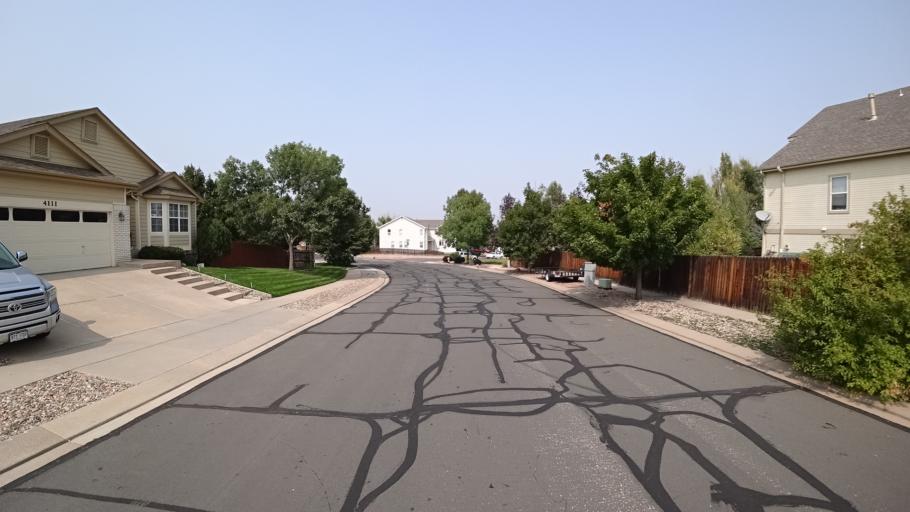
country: US
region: Colorado
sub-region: El Paso County
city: Cimarron Hills
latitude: 38.9178
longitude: -104.7508
